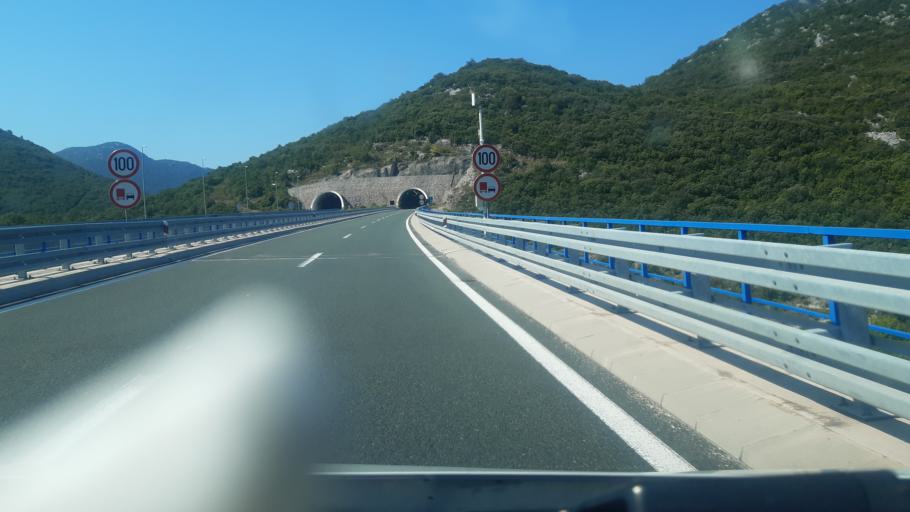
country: HR
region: Dubrovacko-Neretvanska
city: Komin
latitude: 43.1177
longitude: 17.4826
